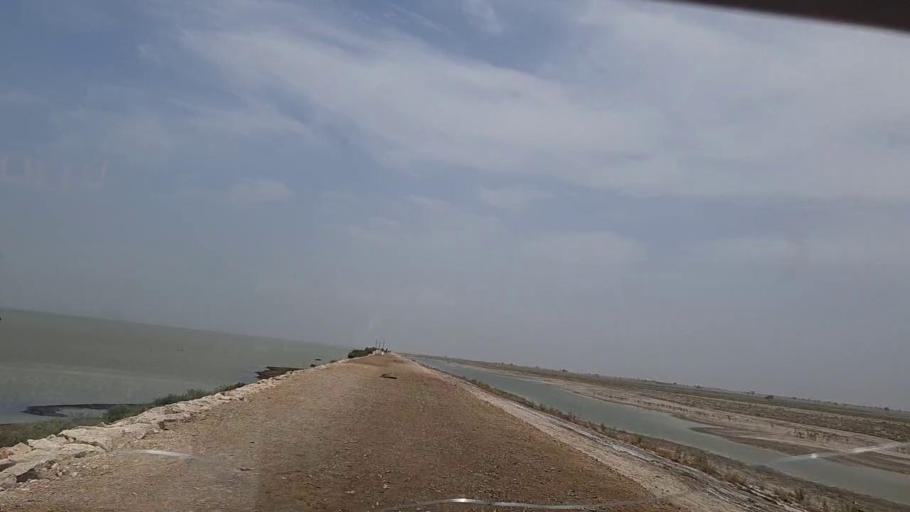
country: PK
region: Sindh
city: Sehwan
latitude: 26.4176
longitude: 67.7445
